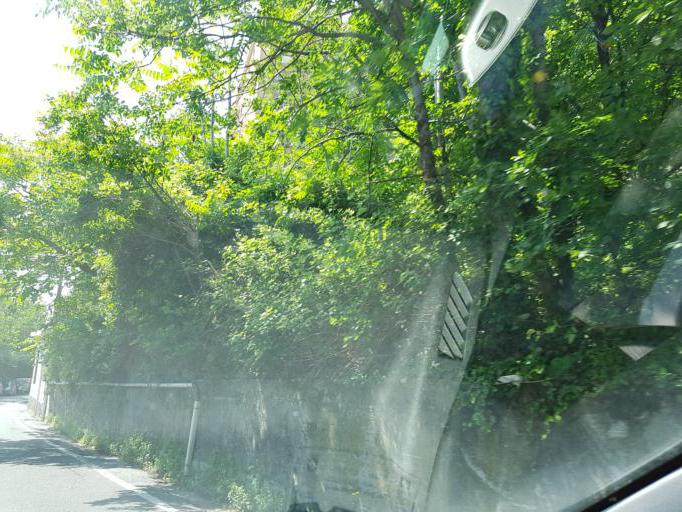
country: IT
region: Liguria
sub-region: Provincia di Genova
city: Genoa
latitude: 44.4233
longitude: 8.9175
